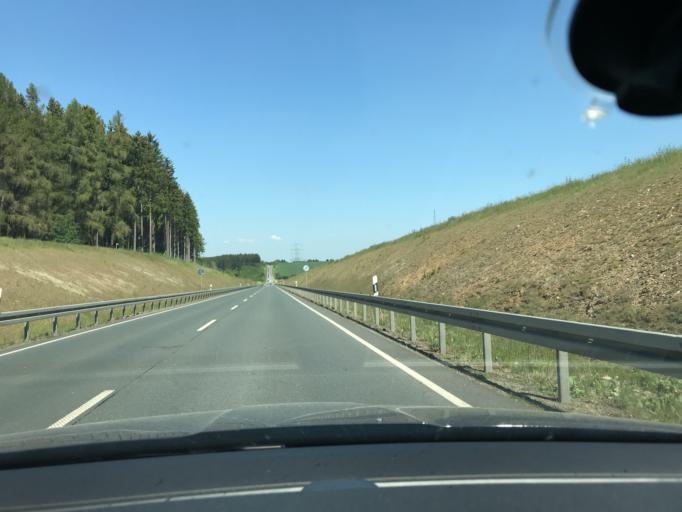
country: DE
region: Saxony
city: Dorfchemnitz
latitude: 50.6763
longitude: 12.8055
